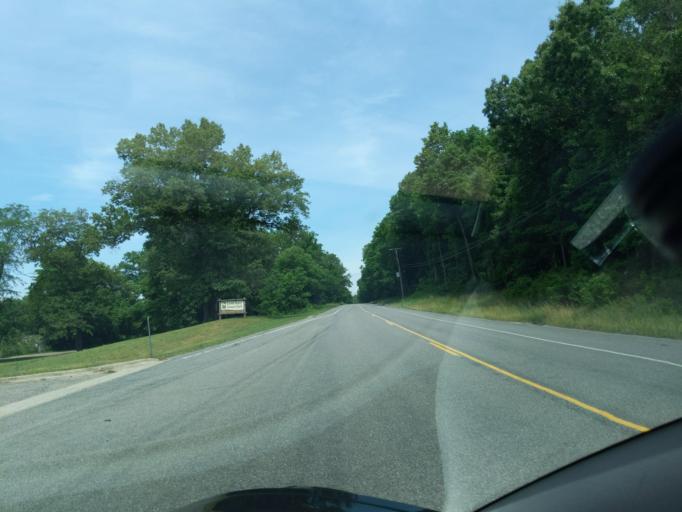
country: US
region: Michigan
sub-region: Kent County
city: Forest Hills
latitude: 42.9635
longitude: -85.4858
